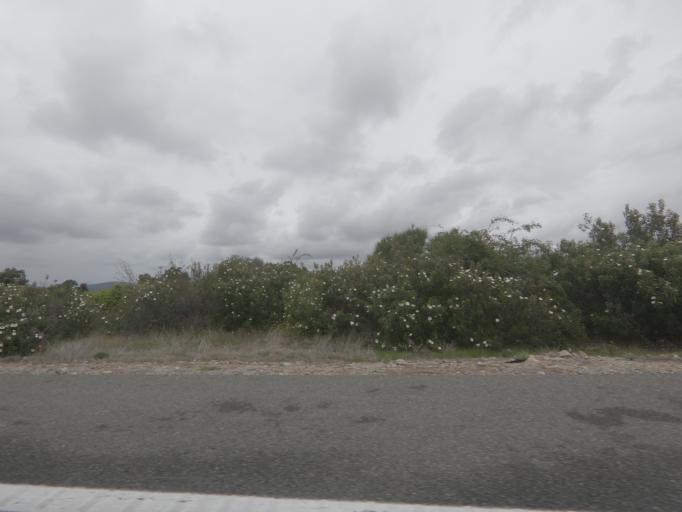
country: ES
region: Extremadura
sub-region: Provincia de Caceres
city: Aldeanueva del Camino
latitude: 40.2528
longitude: -5.9438
